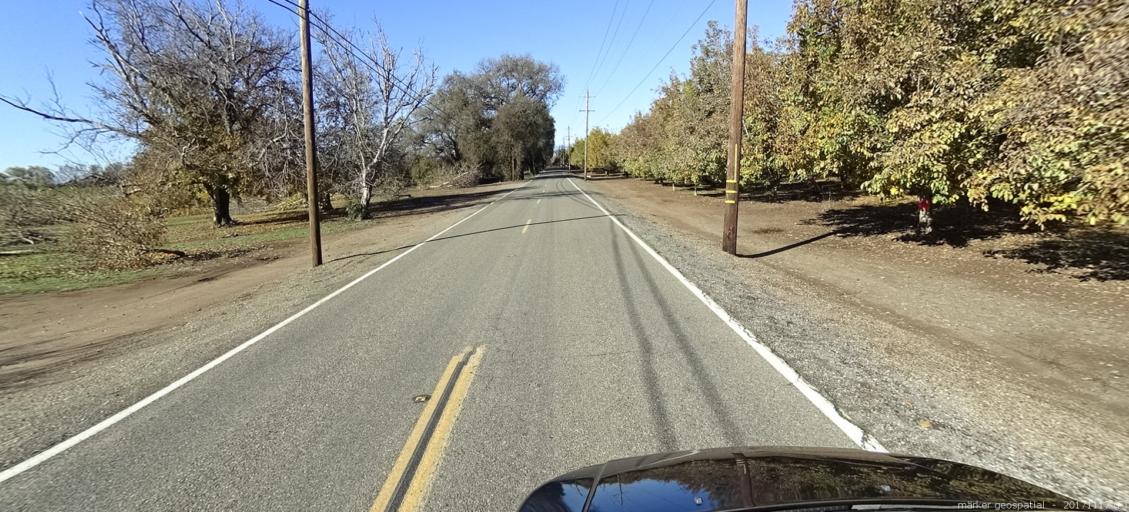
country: US
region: California
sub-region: Shasta County
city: Cottonwood
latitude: 40.4156
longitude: -122.2066
